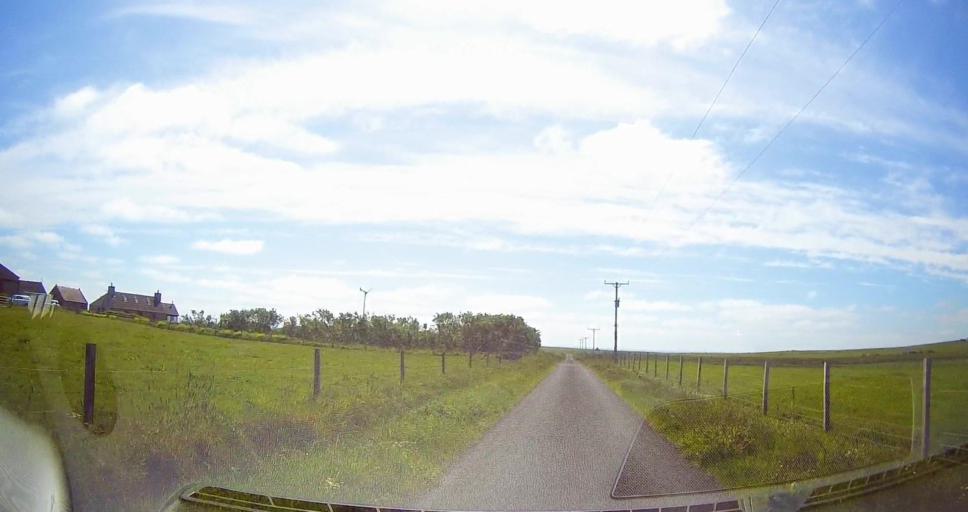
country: GB
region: Scotland
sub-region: Orkney Islands
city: Kirkwall
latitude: 58.8302
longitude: -2.8976
